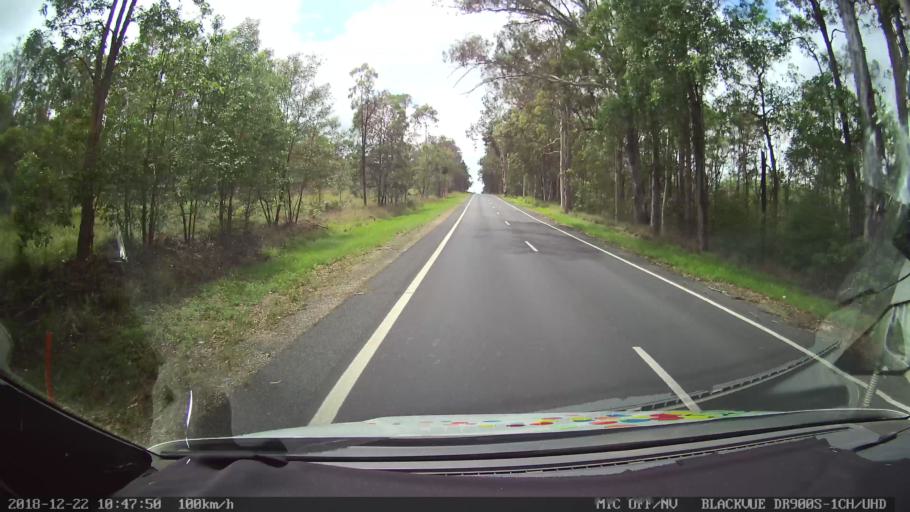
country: AU
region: New South Wales
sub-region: Clarence Valley
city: South Grafton
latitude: -29.6768
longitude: 152.8450
